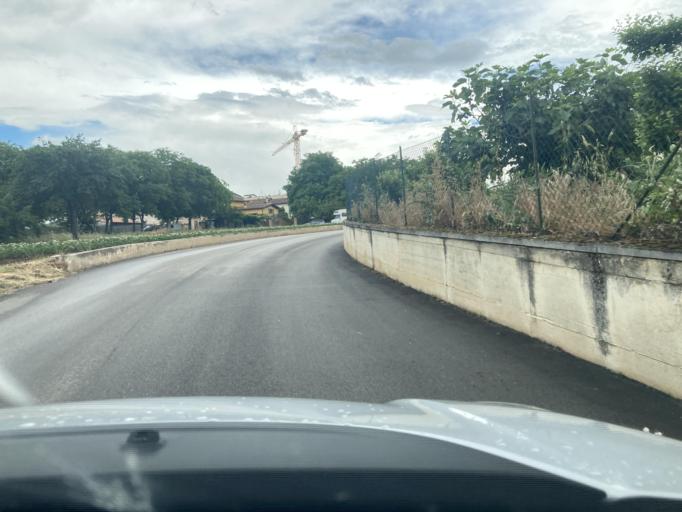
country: IT
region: Abruzzo
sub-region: Provincia dell' Aquila
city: San Demetrio Ne' Vestini
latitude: 42.2935
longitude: 13.5548
